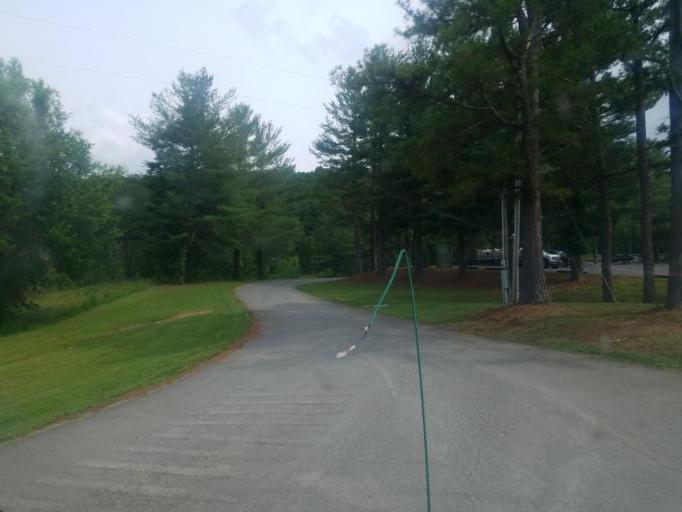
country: US
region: Kentucky
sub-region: Edmonson County
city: Brownsville
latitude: 37.3202
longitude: -86.1319
